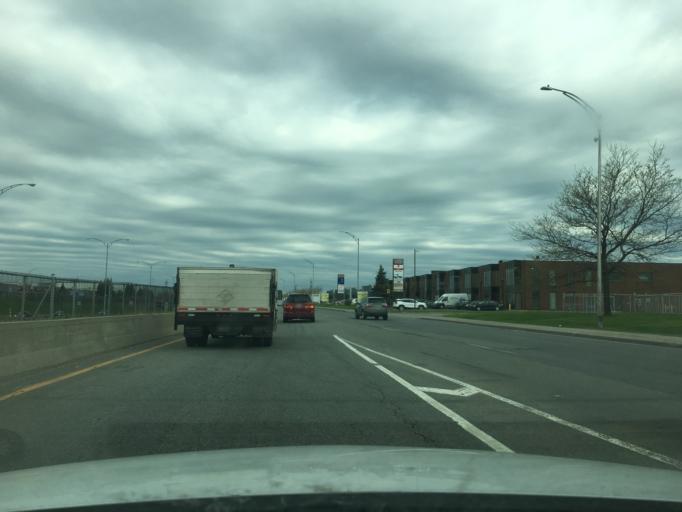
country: CA
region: Quebec
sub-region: Montreal
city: Saint-Leonard
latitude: 45.6121
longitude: -73.5836
